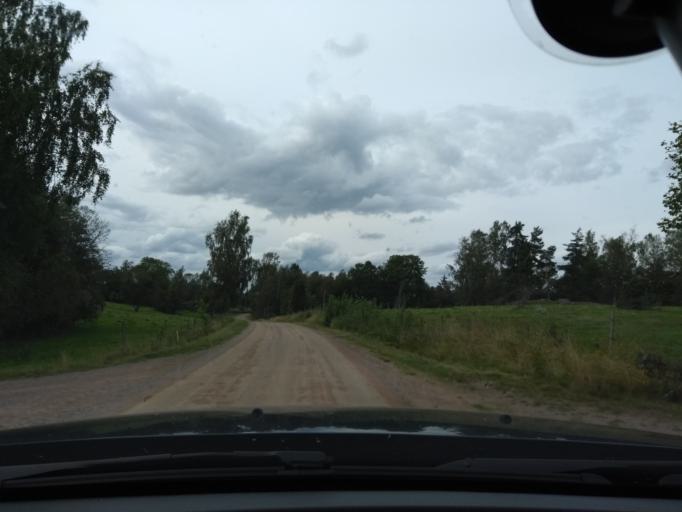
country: SE
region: Joenkoeping
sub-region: Eksjo Kommun
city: Mariannelund
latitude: 57.6314
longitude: 15.6365
